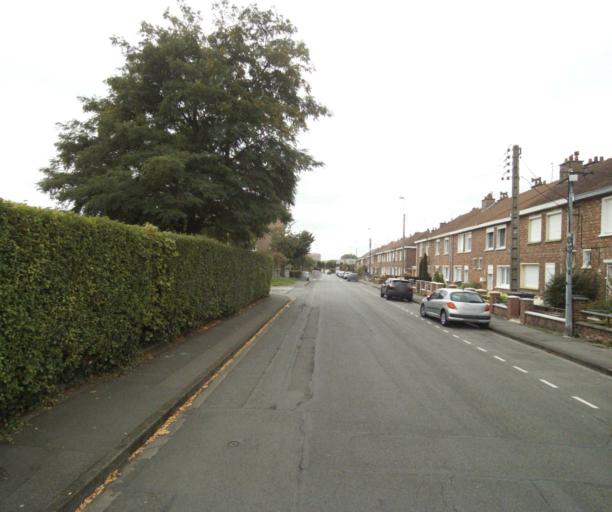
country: FR
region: Nord-Pas-de-Calais
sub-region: Departement du Nord
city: Ronchin
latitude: 50.6018
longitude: 3.0855
